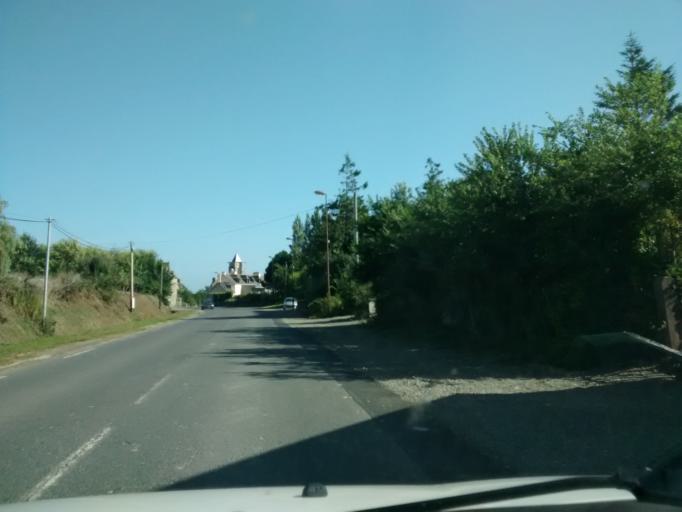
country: FR
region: Brittany
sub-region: Departement des Cotes-d'Armor
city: Pleumeur-Gautier
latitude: 48.8264
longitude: -3.1849
